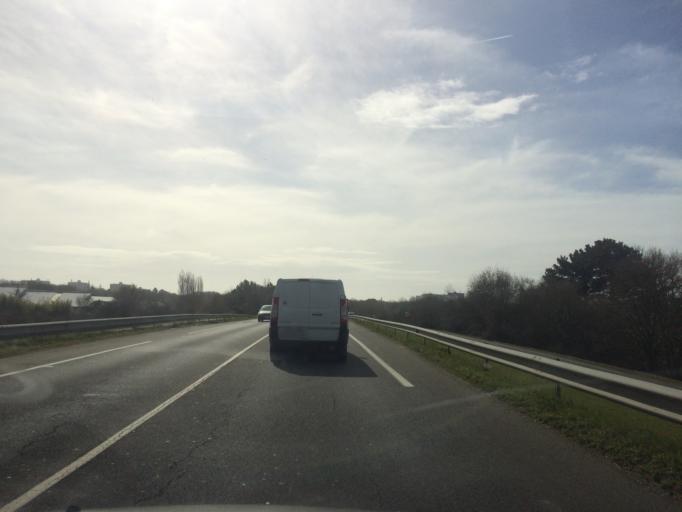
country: FR
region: Pays de la Loire
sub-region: Departement de la Loire-Atlantique
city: Saint-Nazaire
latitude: 47.2785
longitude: -2.2485
